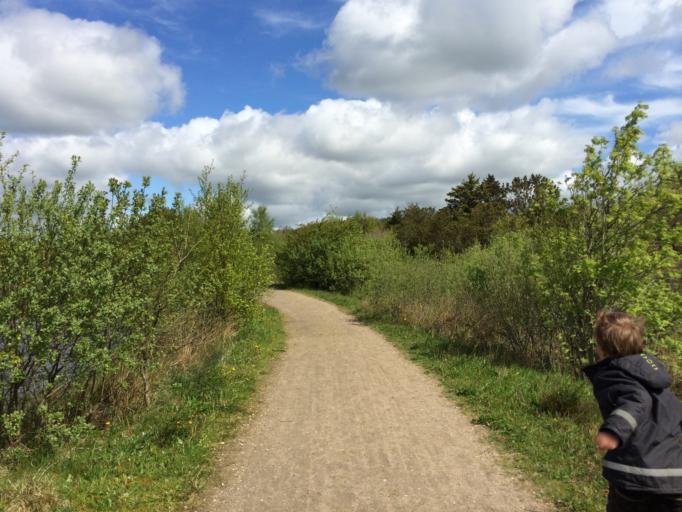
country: DK
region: Central Jutland
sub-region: Holstebro Kommune
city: Holstebro
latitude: 56.2258
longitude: 8.6189
